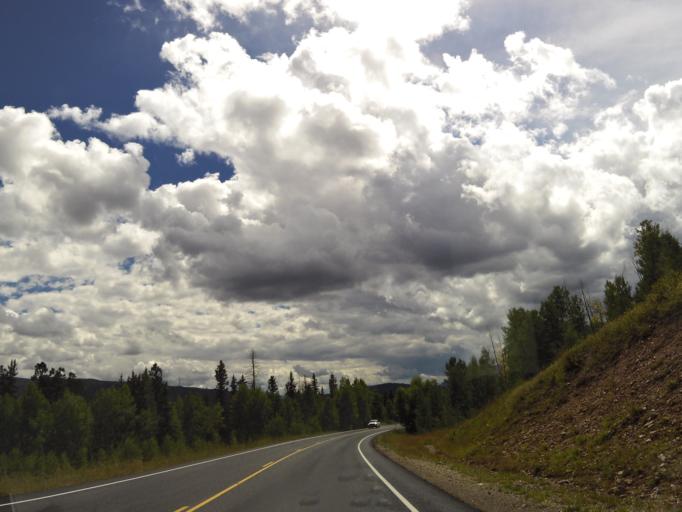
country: US
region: Colorado
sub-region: San Juan County
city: Silverton
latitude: 37.6620
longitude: -107.7979
